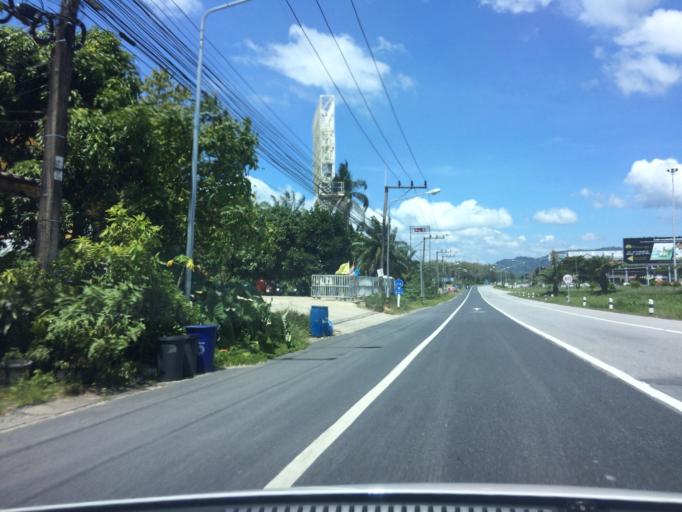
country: TH
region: Phangnga
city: Thai Mueang
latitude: 8.2441
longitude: 98.2976
